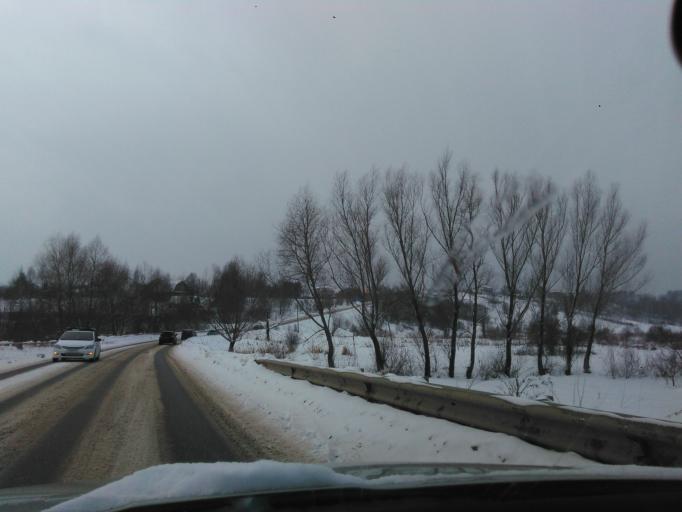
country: RU
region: Moskovskaya
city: Yakhroma
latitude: 56.2695
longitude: 37.4881
